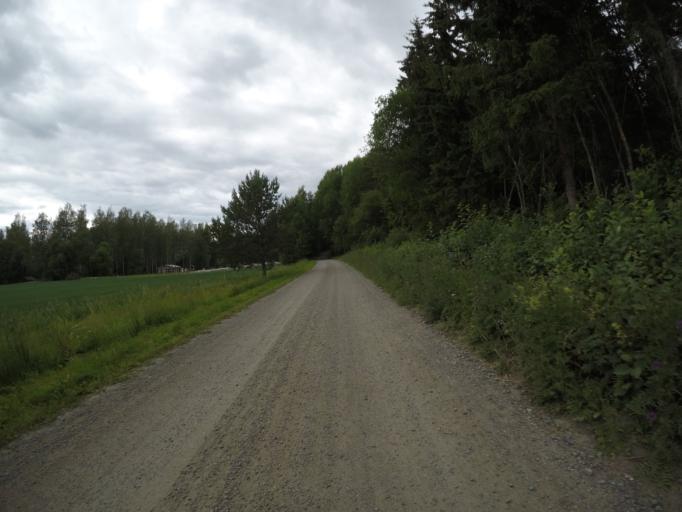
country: FI
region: Haeme
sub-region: Haemeenlinna
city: Haemeenlinna
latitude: 60.9767
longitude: 24.4550
